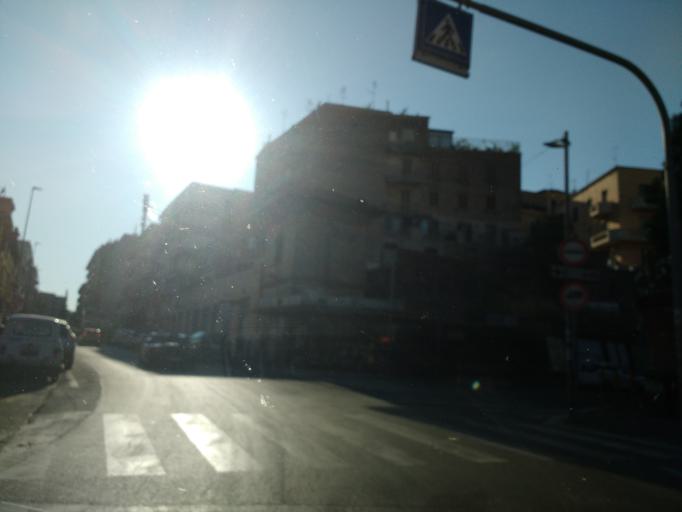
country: IT
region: Latium
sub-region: Citta metropolitana di Roma Capitale
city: Tivoli
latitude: 41.9598
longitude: 12.8019
